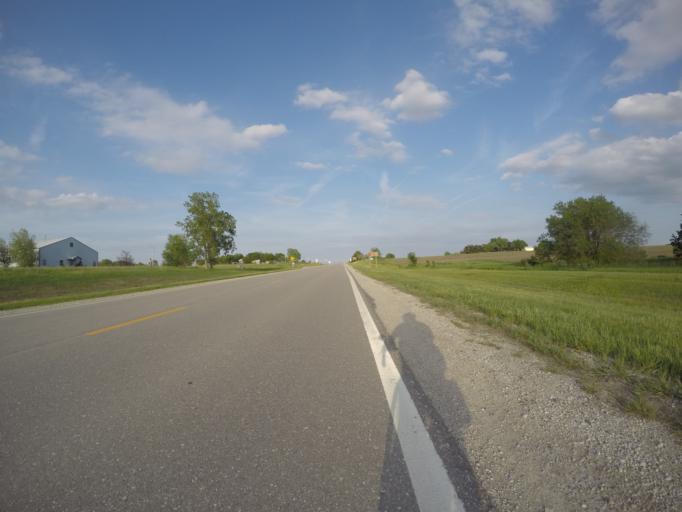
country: US
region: Kansas
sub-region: Pottawatomie County
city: Westmoreland
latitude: 39.4282
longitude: -96.6094
